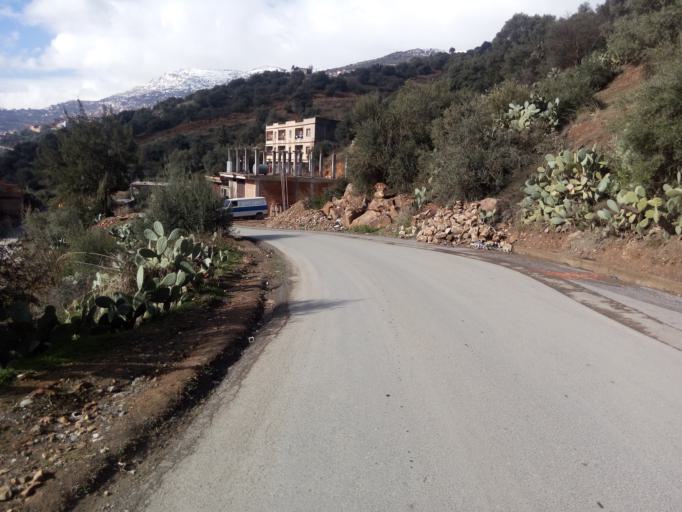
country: DZ
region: Tizi Ouzou
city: Chemini
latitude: 36.6079
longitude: 4.6469
